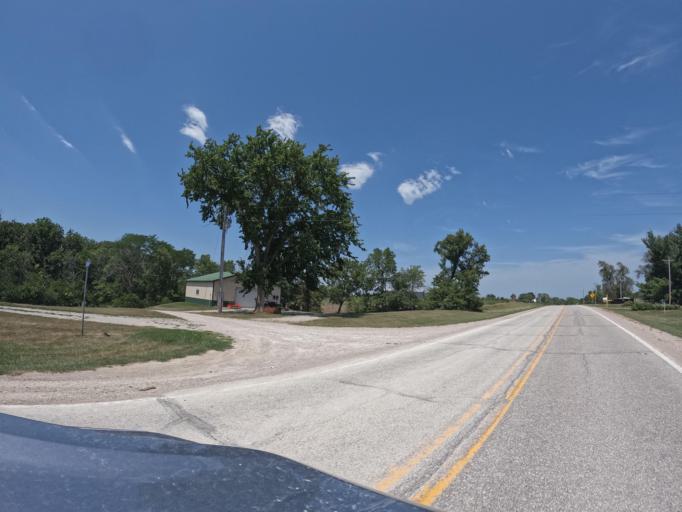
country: US
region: Iowa
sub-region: Henry County
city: Mount Pleasant
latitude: 40.9428
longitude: -91.6146
